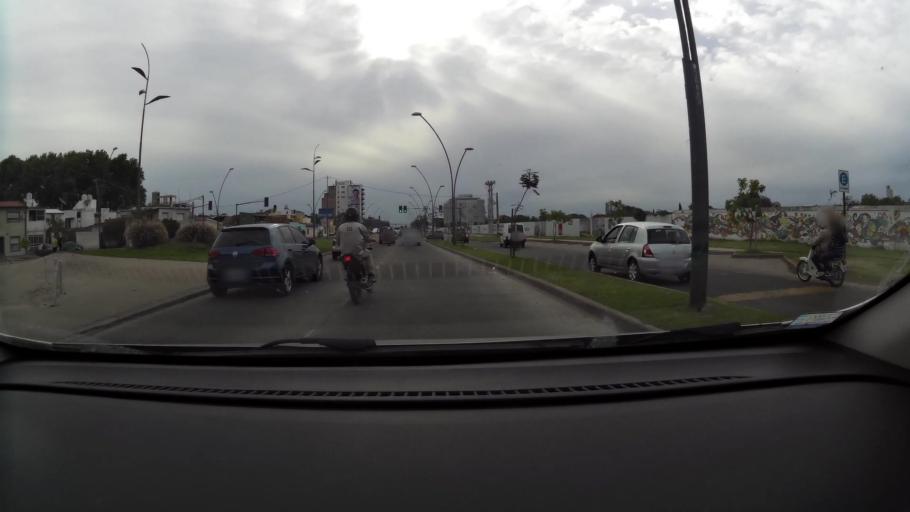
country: AR
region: Santa Fe
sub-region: Departamento de Rosario
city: Rosario
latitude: -32.9218
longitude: -60.6687
